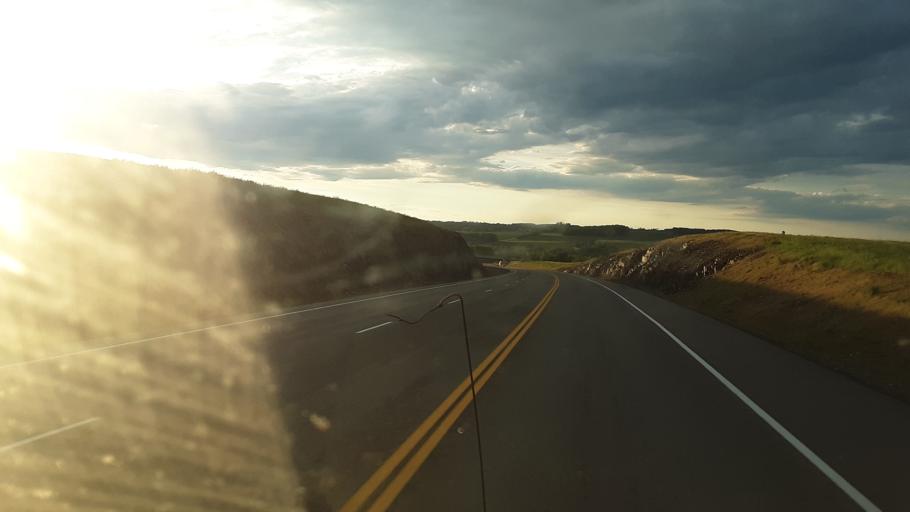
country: US
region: Maine
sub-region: Aroostook County
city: Presque Isle
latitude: 46.6860
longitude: -67.9756
